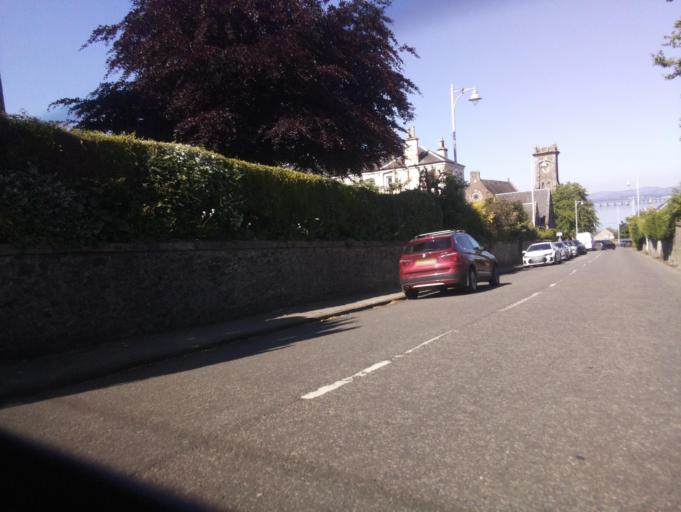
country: GB
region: Scotland
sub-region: Fife
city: Newport-On-Tay
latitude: 56.4399
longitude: -2.9387
